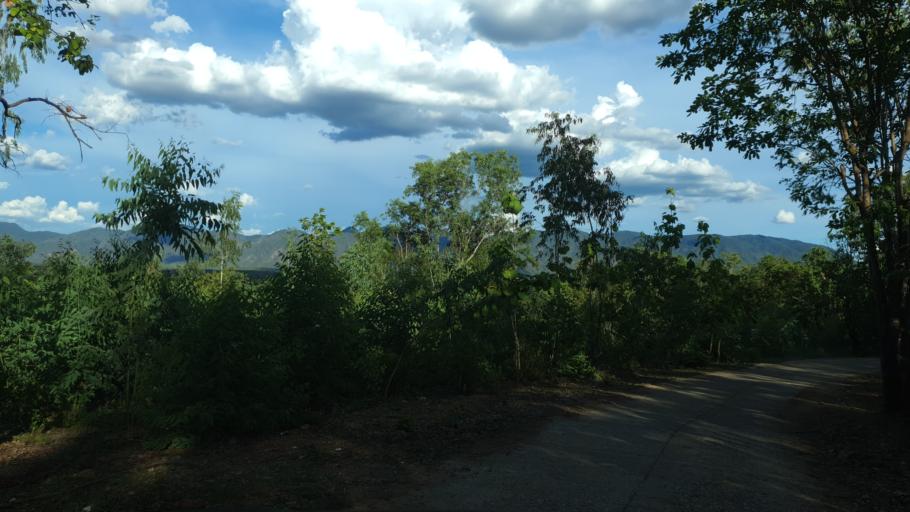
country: TH
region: Lampang
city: Sop Prap
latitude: 17.8794
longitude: 99.2975
